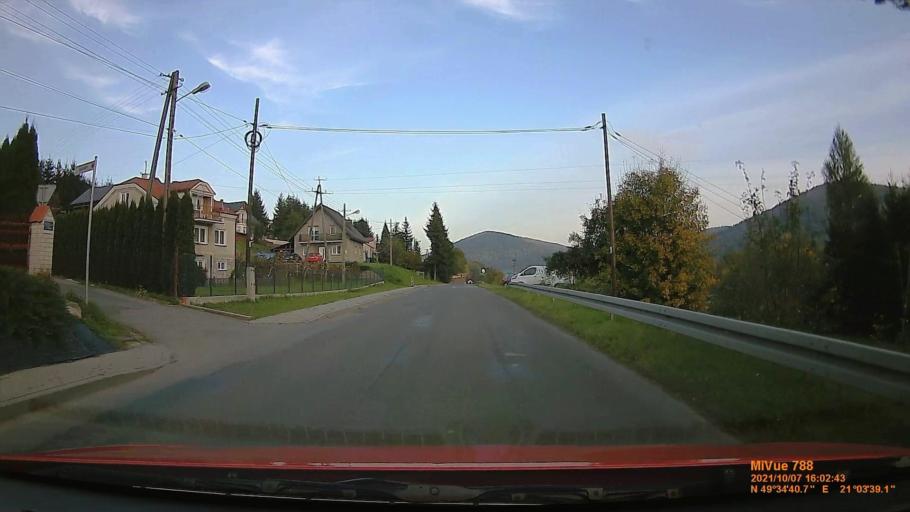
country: PL
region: Lesser Poland Voivodeship
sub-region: Powiat gorlicki
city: Ropa
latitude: 49.5781
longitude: 21.0609
